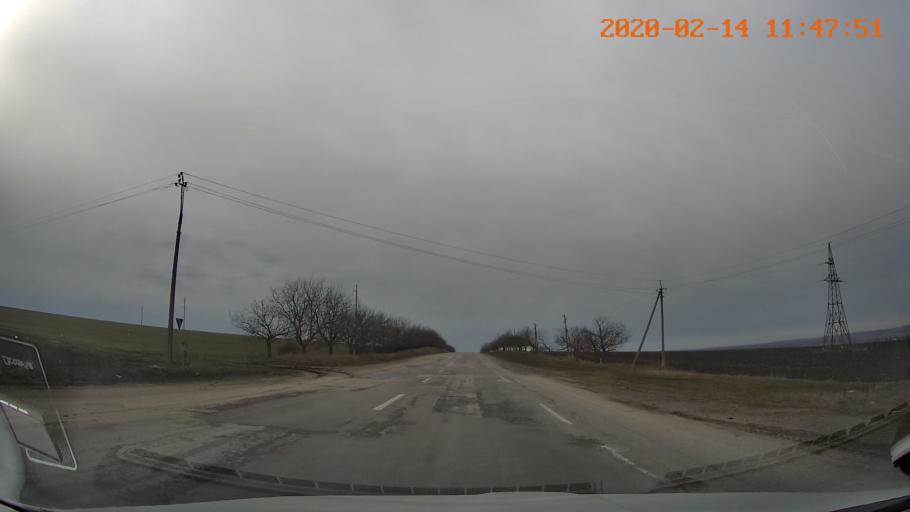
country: MD
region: Briceni
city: Briceni
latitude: 48.3128
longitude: 26.9614
